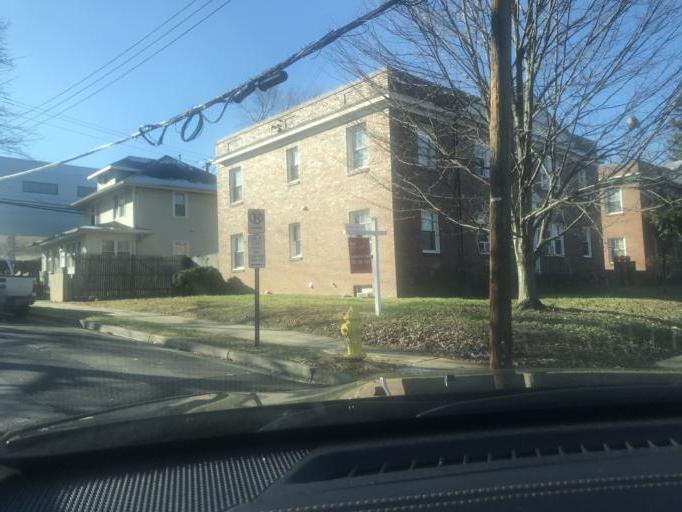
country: US
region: Washington, D.C.
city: Washington, D.C.
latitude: 38.8541
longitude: -77.0575
